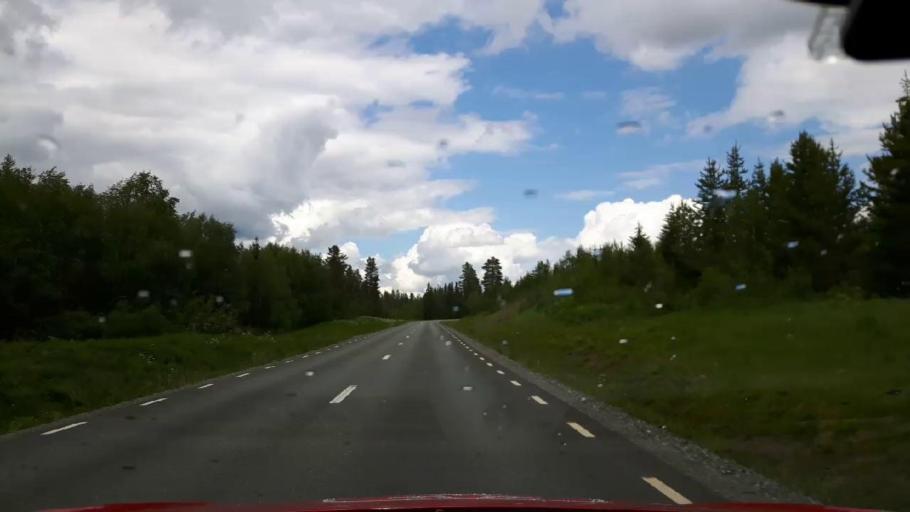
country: SE
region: Jaemtland
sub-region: Krokoms Kommun
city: Krokom
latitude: 63.5885
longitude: 14.2949
